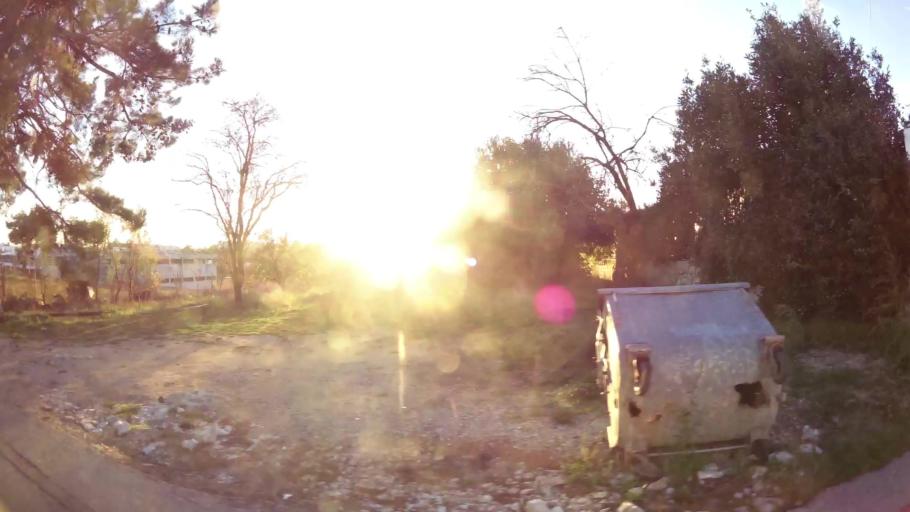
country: GR
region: Attica
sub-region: Nomarchia Anatolikis Attikis
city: Agios Stefanos
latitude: 38.1465
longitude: 23.8419
